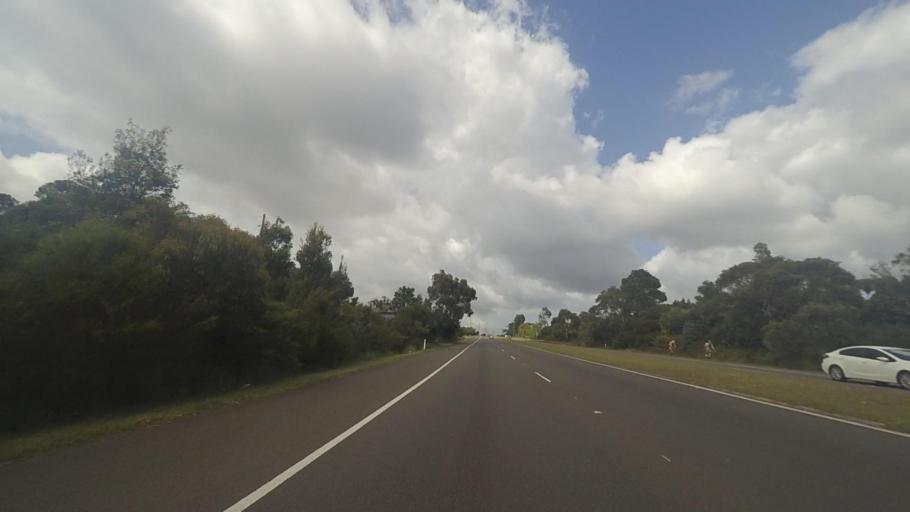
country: AU
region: New South Wales
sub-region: Sutherland Shire
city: Heathcote
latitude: -34.0937
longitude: 151.0013
